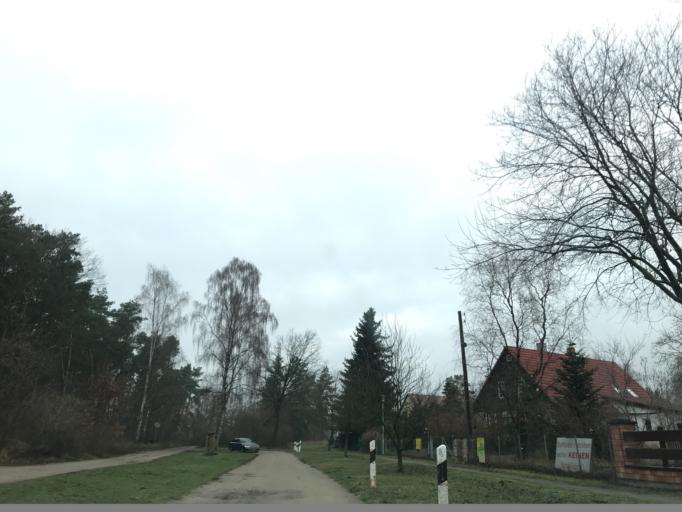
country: DE
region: Brandenburg
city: Kremmen
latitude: 52.7339
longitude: 12.9852
